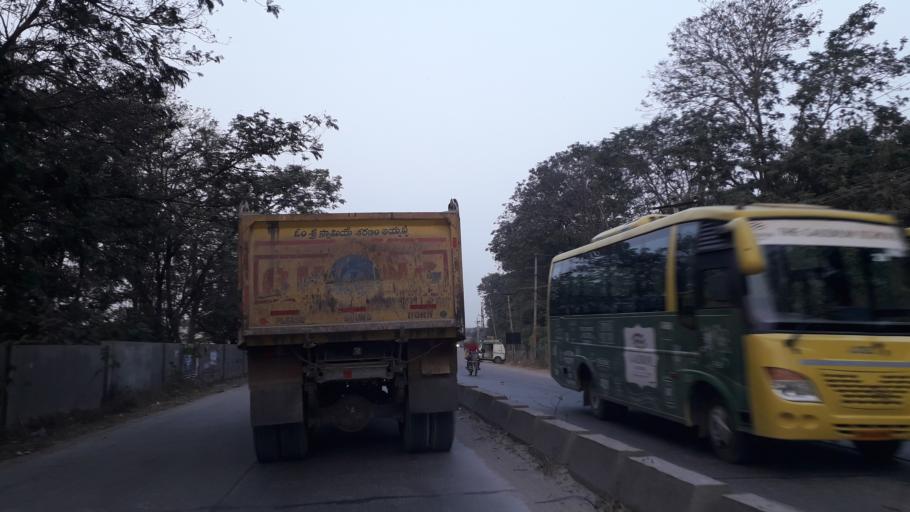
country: IN
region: Telangana
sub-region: Medak
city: Patancheru
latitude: 17.5293
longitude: 78.2538
